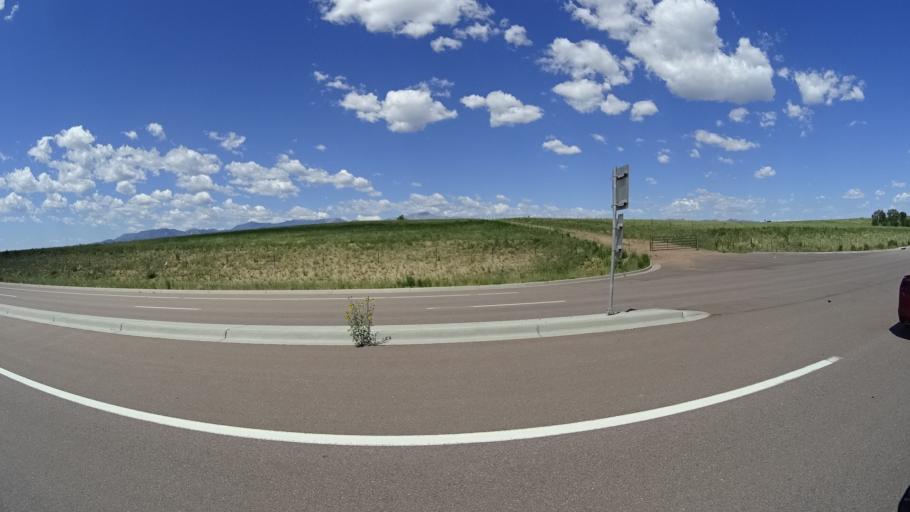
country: US
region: Colorado
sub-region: El Paso County
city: Cimarron Hills
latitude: 38.8438
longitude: -104.6827
